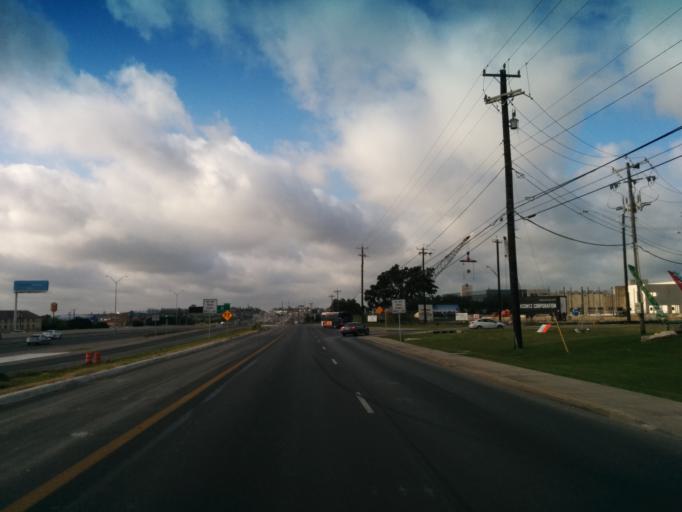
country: US
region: Texas
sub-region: Bexar County
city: Shavano Park
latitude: 29.5733
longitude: -98.5947
